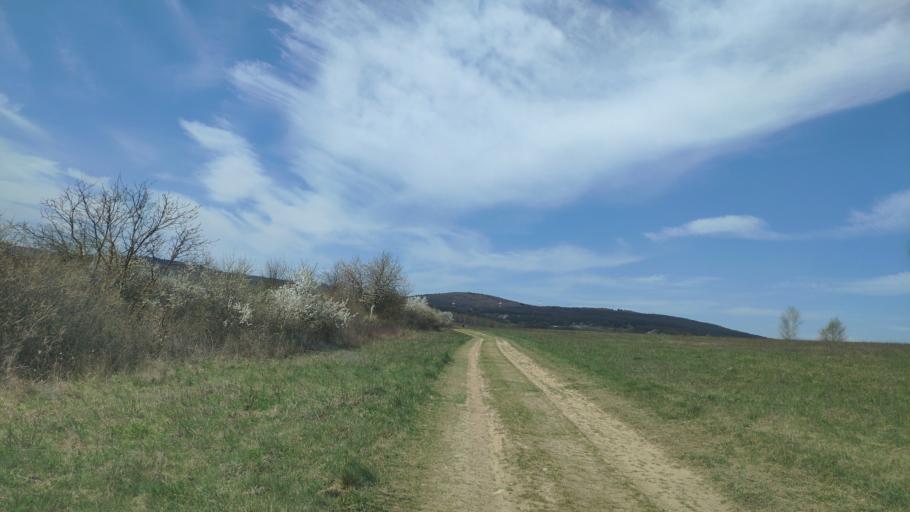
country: SK
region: Kosicky
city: Kosice
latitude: 48.7182
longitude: 21.1988
